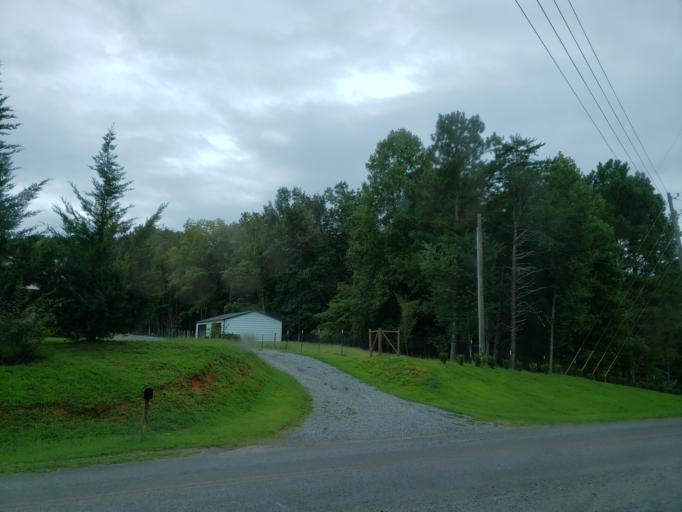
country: US
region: Georgia
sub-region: Gilmer County
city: Ellijay
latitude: 34.6173
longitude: -84.5694
